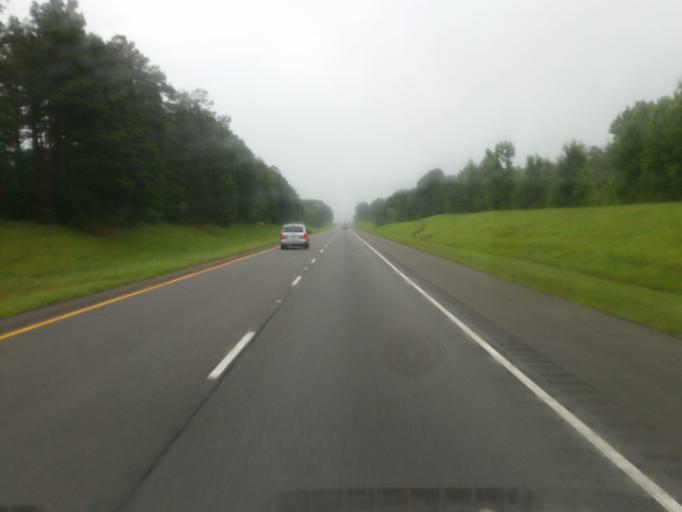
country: US
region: Louisiana
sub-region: Bossier Parish
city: Eastwood
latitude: 32.5418
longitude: -93.5592
